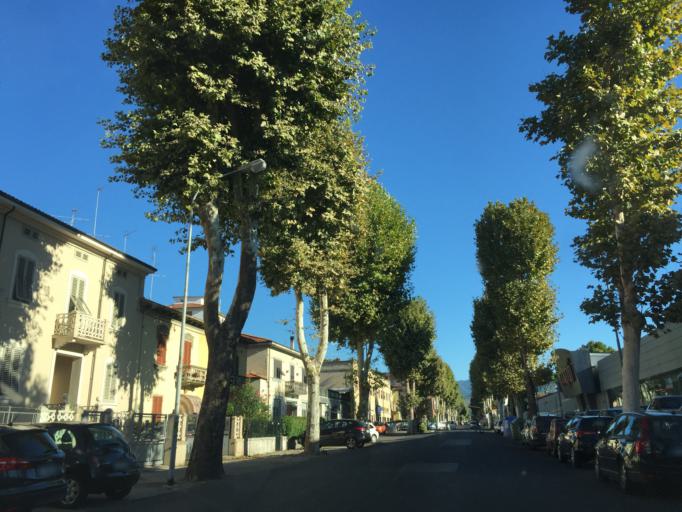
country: IT
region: Tuscany
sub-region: Provincia di Pistoia
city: Pistoia
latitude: 43.9293
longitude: 10.9004
